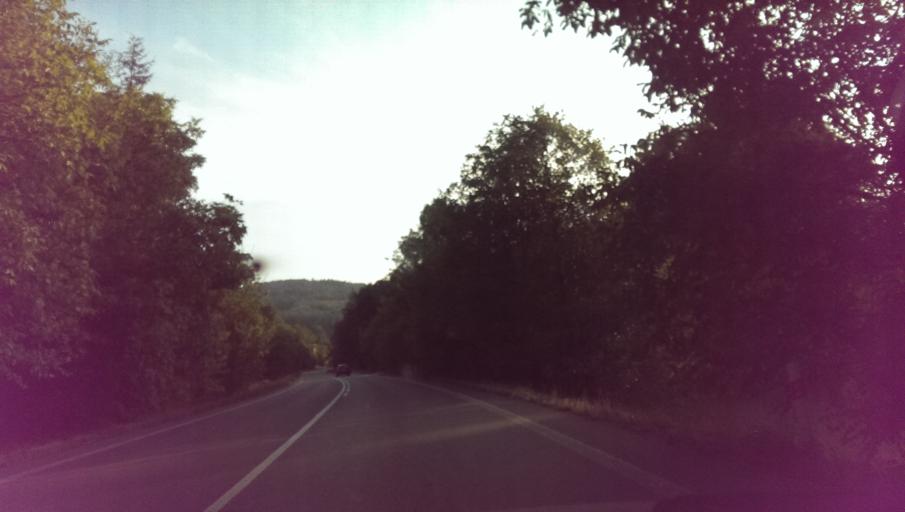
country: CZ
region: Zlin
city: Pozlovice
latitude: 49.1289
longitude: 17.8018
